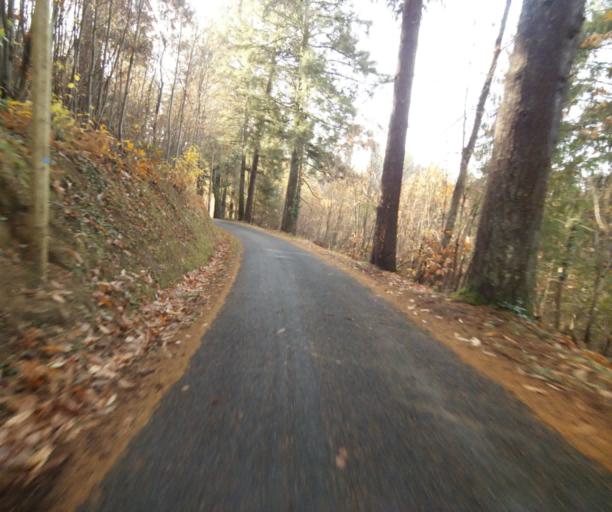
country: FR
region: Limousin
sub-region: Departement de la Correze
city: Sainte-Fortunade
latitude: 45.2180
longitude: 1.7464
